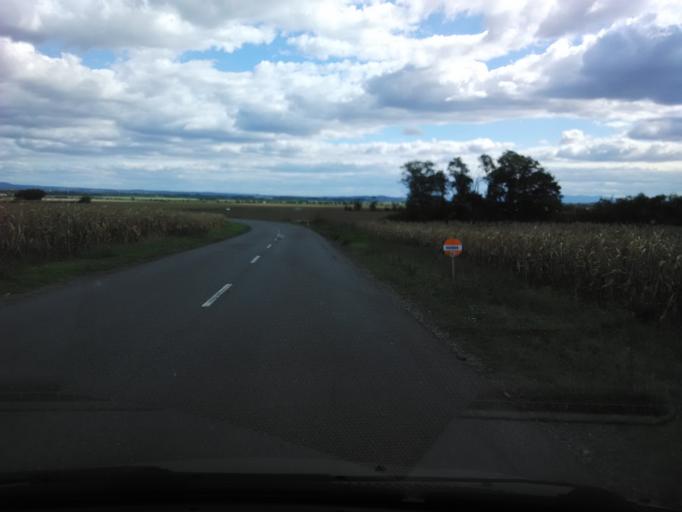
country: SK
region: Nitriansky
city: Tlmace
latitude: 48.2430
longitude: 18.4680
